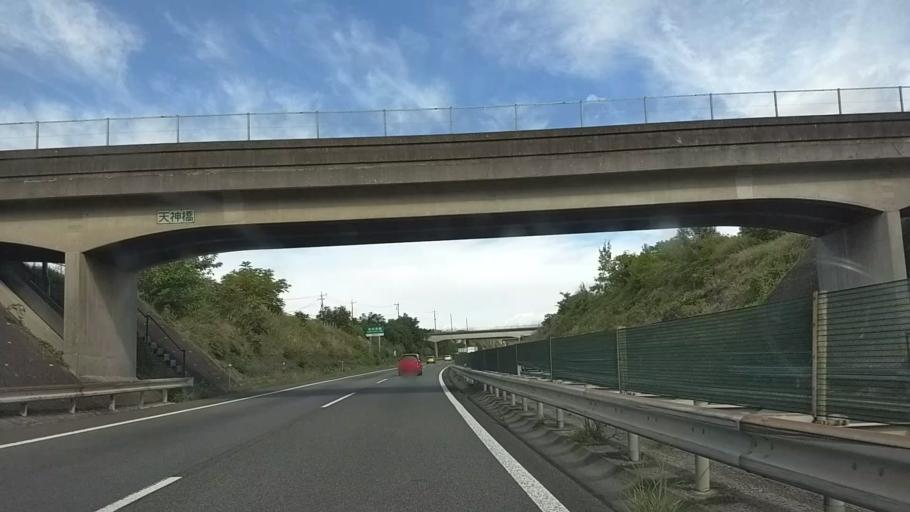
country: JP
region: Yamanashi
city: Nirasaki
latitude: 35.7048
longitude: 138.4760
